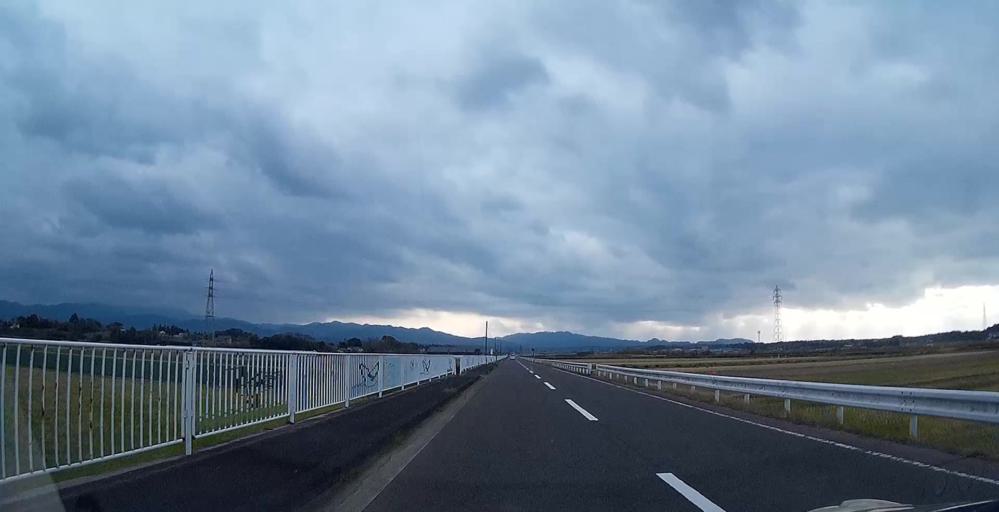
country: JP
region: Kagoshima
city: Izumi
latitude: 32.0900
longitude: 130.2763
